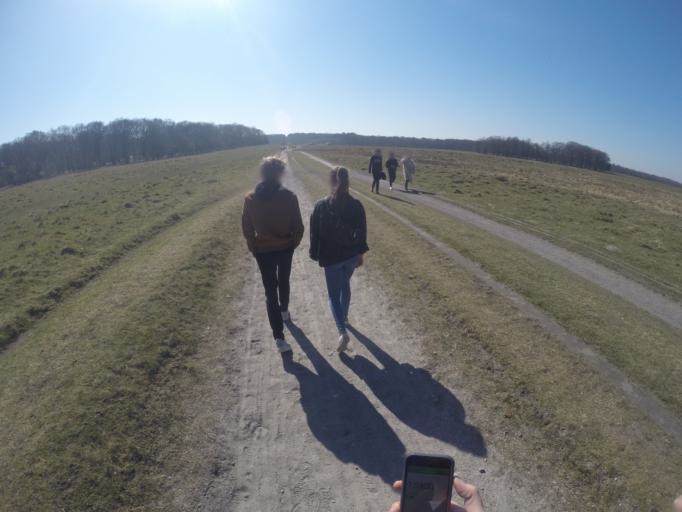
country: DK
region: Capital Region
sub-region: Gentofte Kommune
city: Charlottenlund
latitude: 55.7919
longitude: 12.5671
